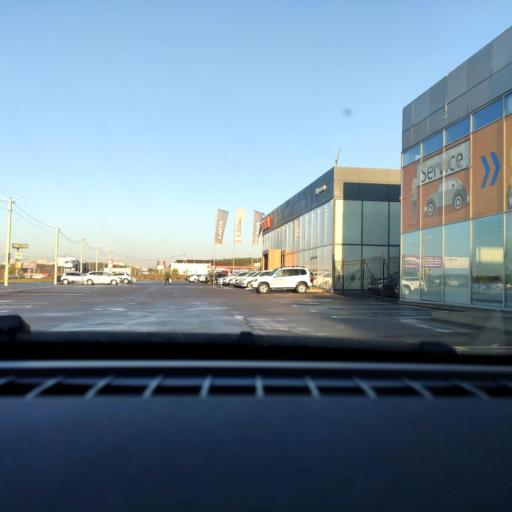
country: RU
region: Voronezj
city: Somovo
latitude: 51.6798
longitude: 39.2897
